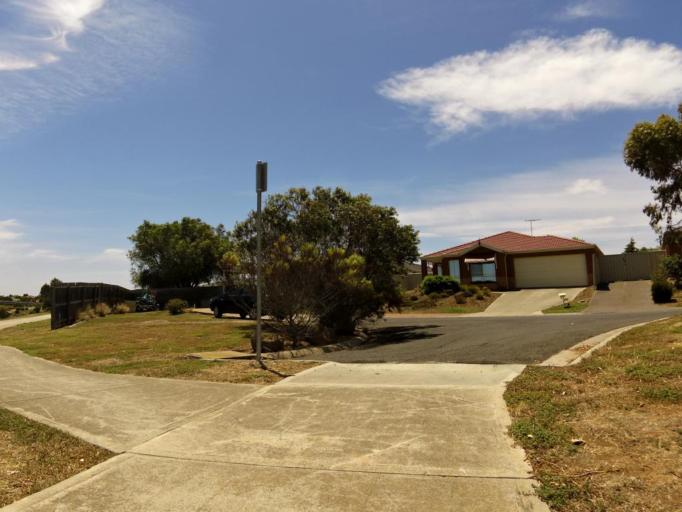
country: AU
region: Victoria
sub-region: Wyndham
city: Williams Landing
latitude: -37.8584
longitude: 144.7184
